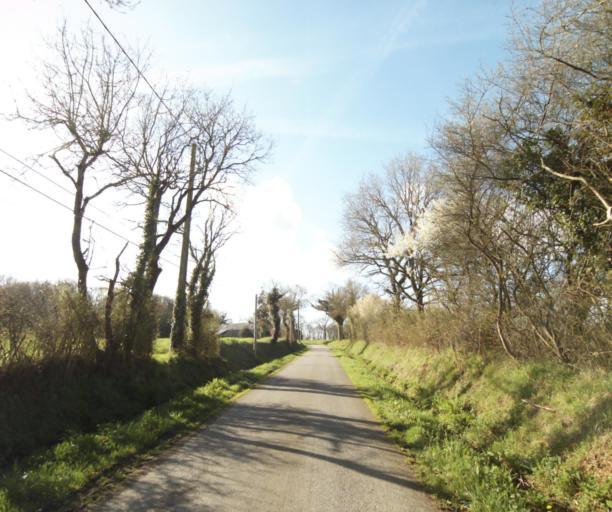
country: FR
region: Pays de la Loire
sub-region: Departement de la Loire-Atlantique
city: Bouvron
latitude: 47.4003
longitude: -1.8480
